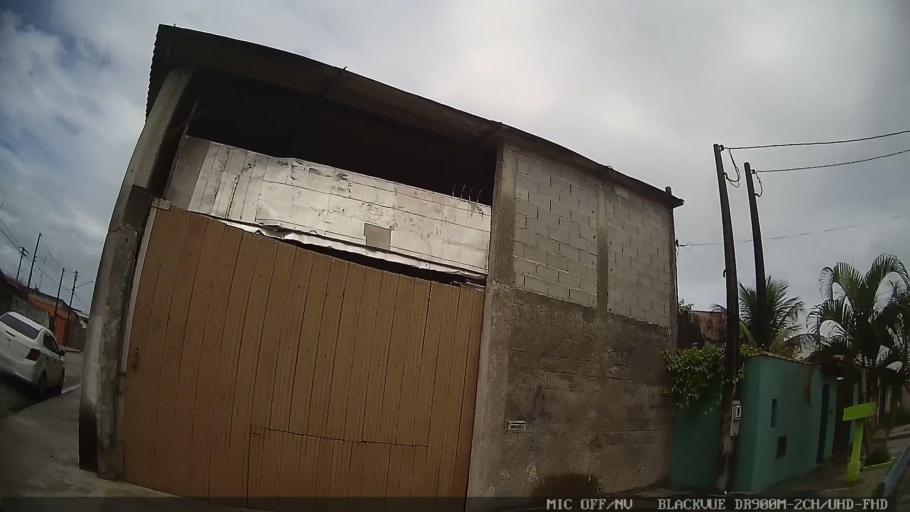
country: BR
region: Sao Paulo
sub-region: Itanhaem
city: Itanhaem
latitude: -24.1718
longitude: -46.7834
